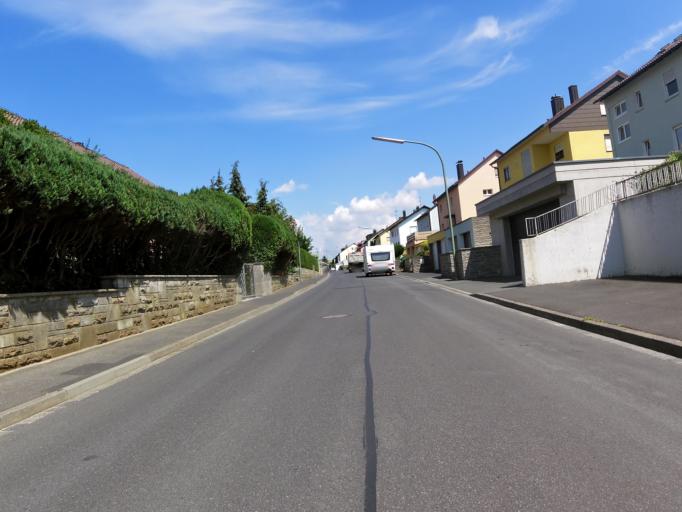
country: DE
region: Bavaria
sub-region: Regierungsbezirk Unterfranken
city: Estenfeld
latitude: 49.8236
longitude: 9.9726
